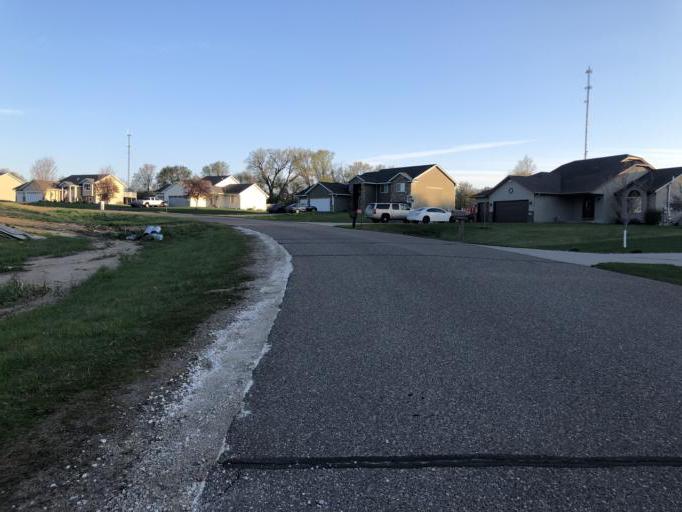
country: US
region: Minnesota
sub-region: Sherburne County
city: Becker
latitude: 45.4247
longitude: -93.8333
